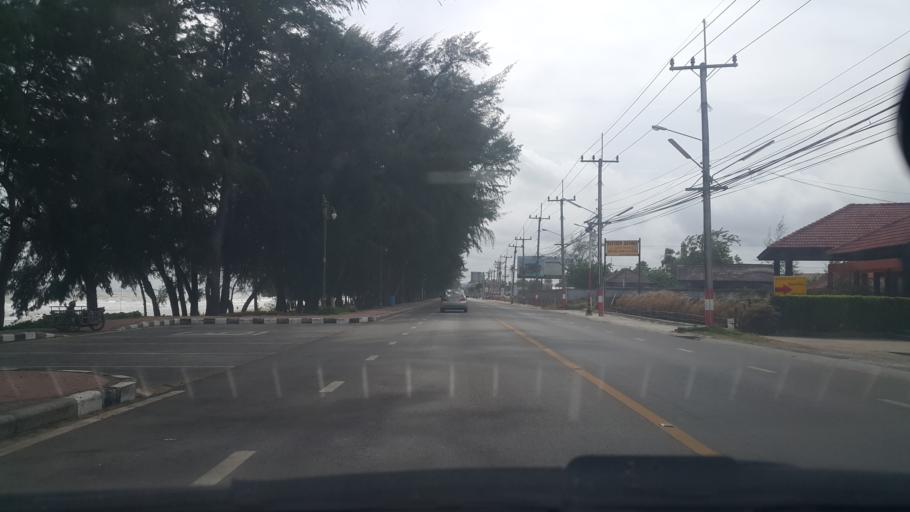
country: TH
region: Rayong
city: Rayong
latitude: 12.6246
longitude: 101.3586
